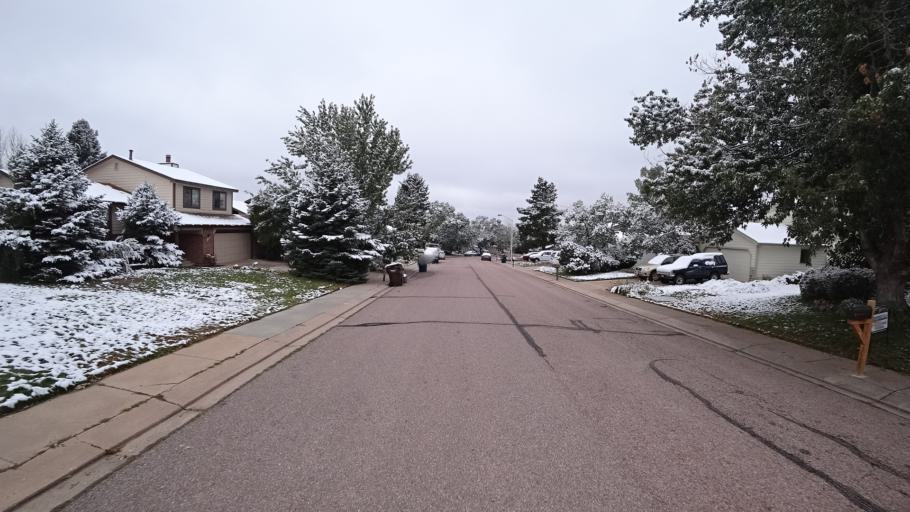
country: US
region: Colorado
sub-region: El Paso County
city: Colorado Springs
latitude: 38.9233
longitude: -104.7791
